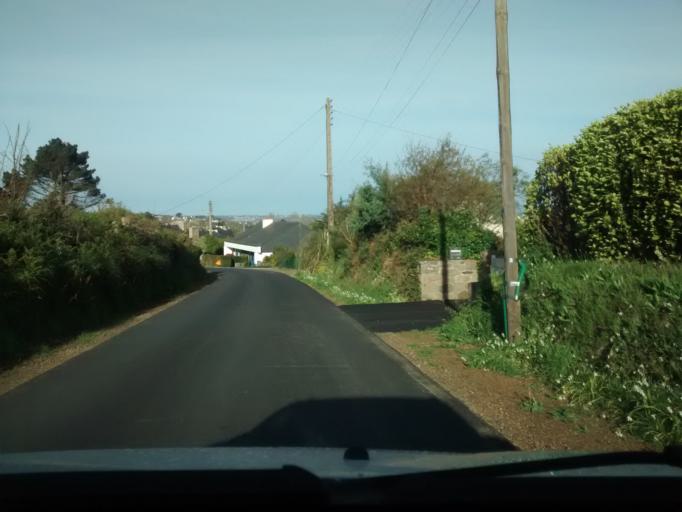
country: FR
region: Brittany
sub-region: Departement des Cotes-d'Armor
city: Penvenan
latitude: 48.8315
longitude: -3.3159
